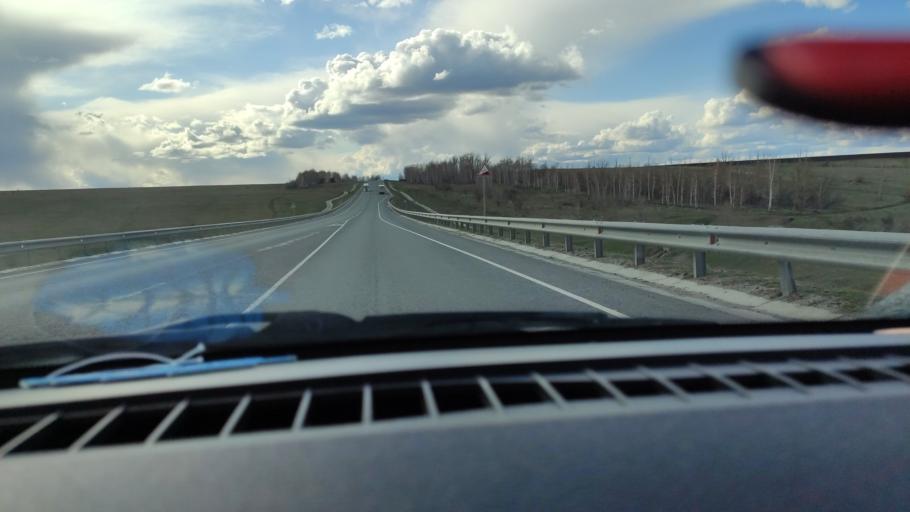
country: RU
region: Saratov
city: Shikhany
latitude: 52.1202
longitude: 47.2654
